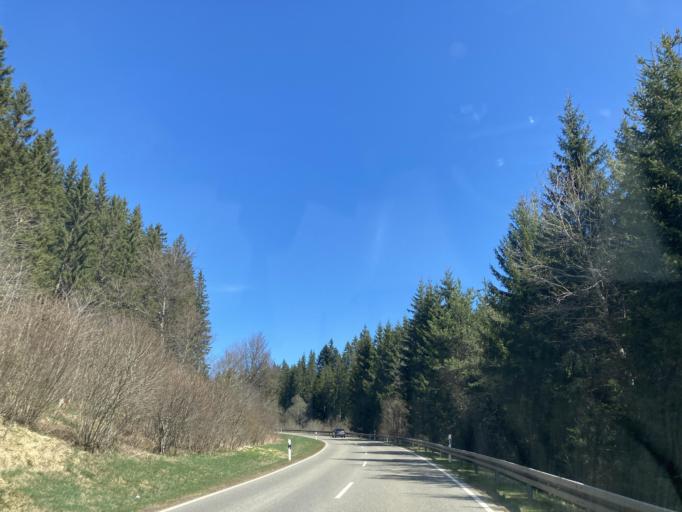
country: DE
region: Baden-Wuerttemberg
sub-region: Freiburg Region
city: Vohrenbach
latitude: 48.0364
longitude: 8.3368
